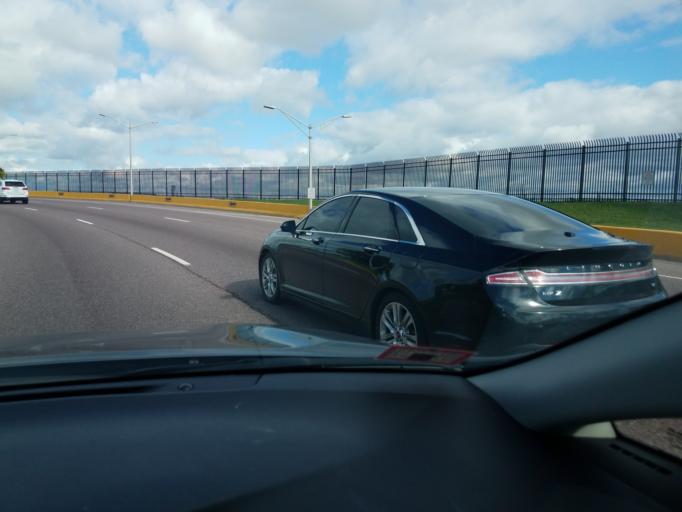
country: US
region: Illinois
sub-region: Cook County
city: Rosemont
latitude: 41.9819
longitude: -87.8963
